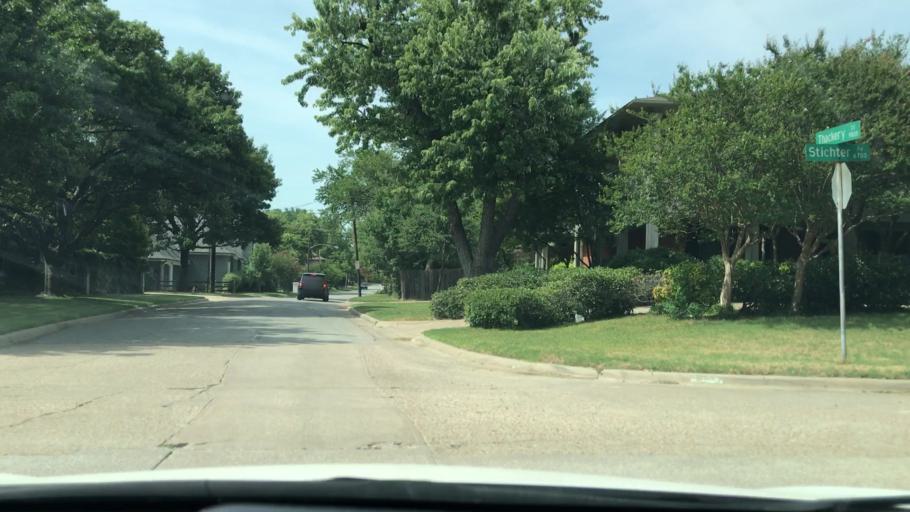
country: US
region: Texas
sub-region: Dallas County
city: University Park
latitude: 32.8811
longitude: -96.7900
